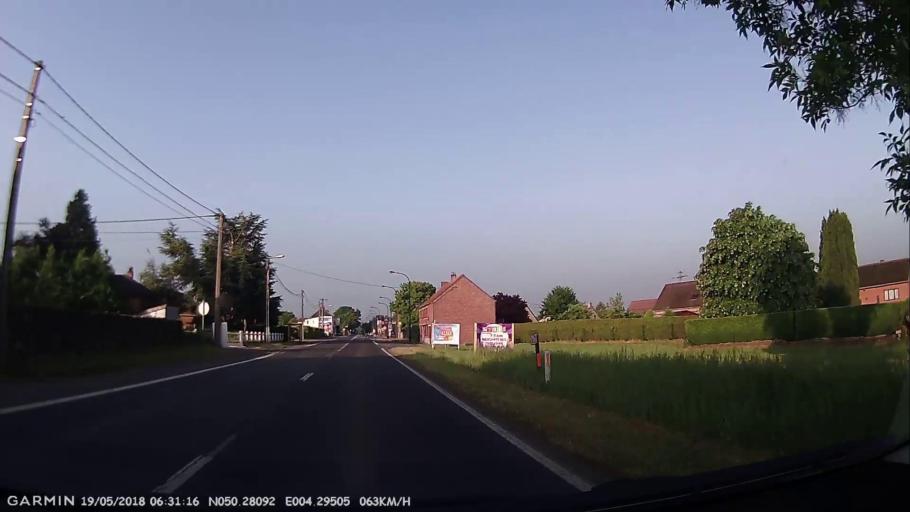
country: BE
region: Wallonia
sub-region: Province du Hainaut
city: Thuin
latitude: 50.2807
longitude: 4.2950
